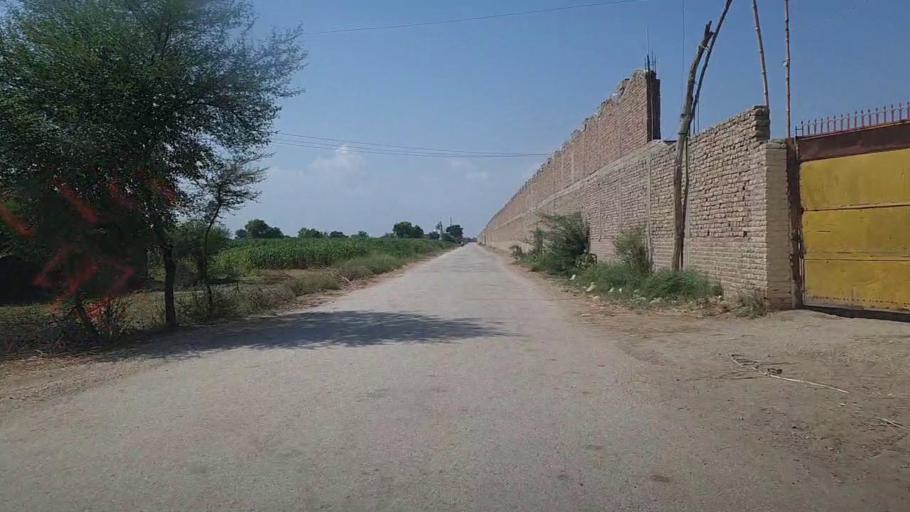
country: PK
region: Sindh
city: Khairpur
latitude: 28.0621
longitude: 69.6462
